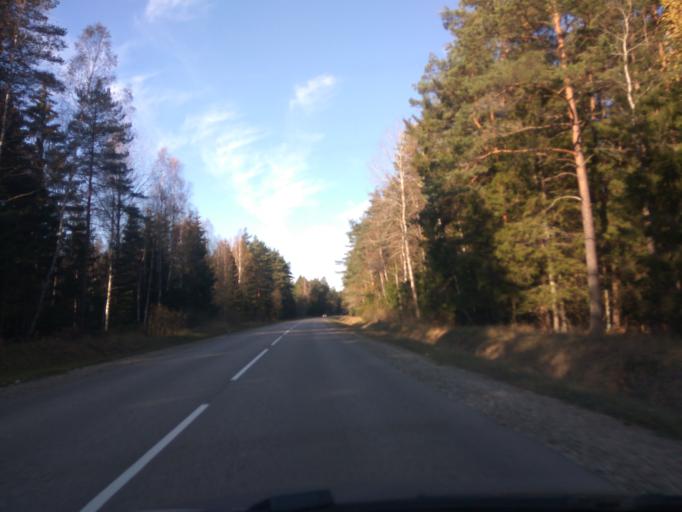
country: LV
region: Ventspils Rajons
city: Piltene
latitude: 57.0809
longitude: 21.7846
